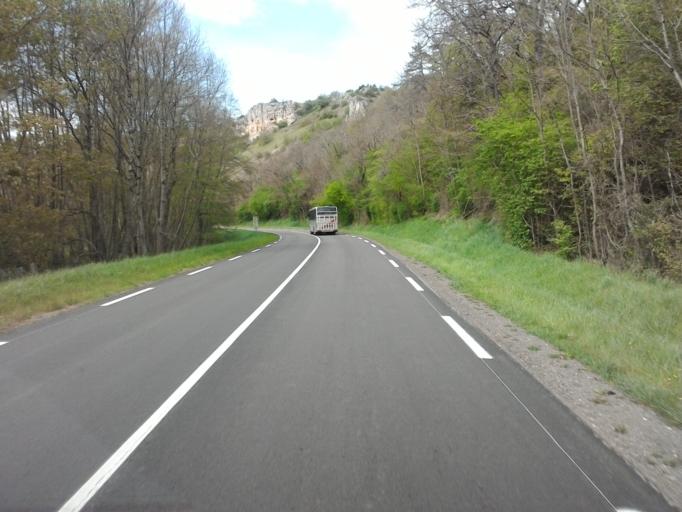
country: FR
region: Bourgogne
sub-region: Departement de l'Yonne
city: Vermenton
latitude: 47.5832
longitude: 3.7785
